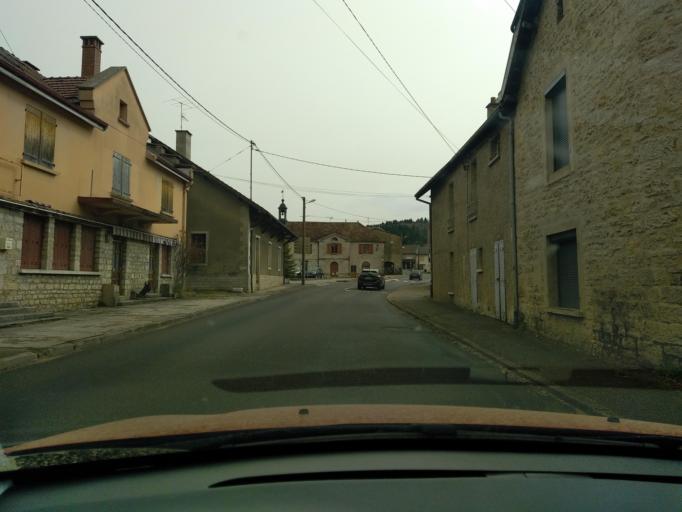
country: FR
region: Franche-Comte
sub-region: Departement du Jura
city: Champagnole
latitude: 46.7517
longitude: 5.8131
